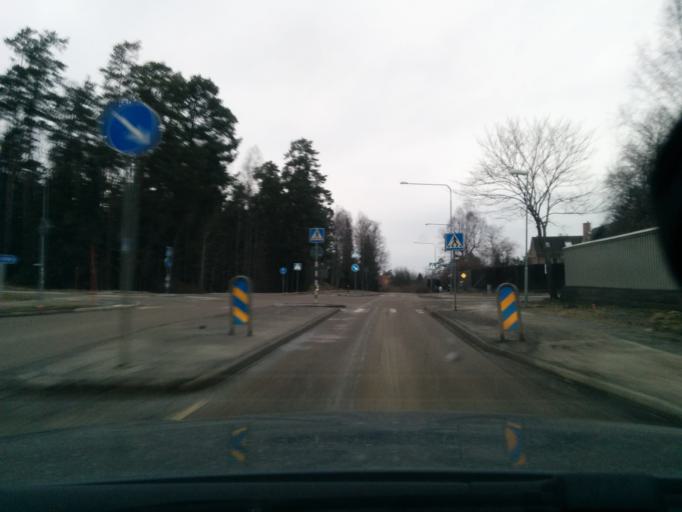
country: SE
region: Stockholm
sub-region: Taby Kommun
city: Taby
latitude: 59.4585
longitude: 18.0353
